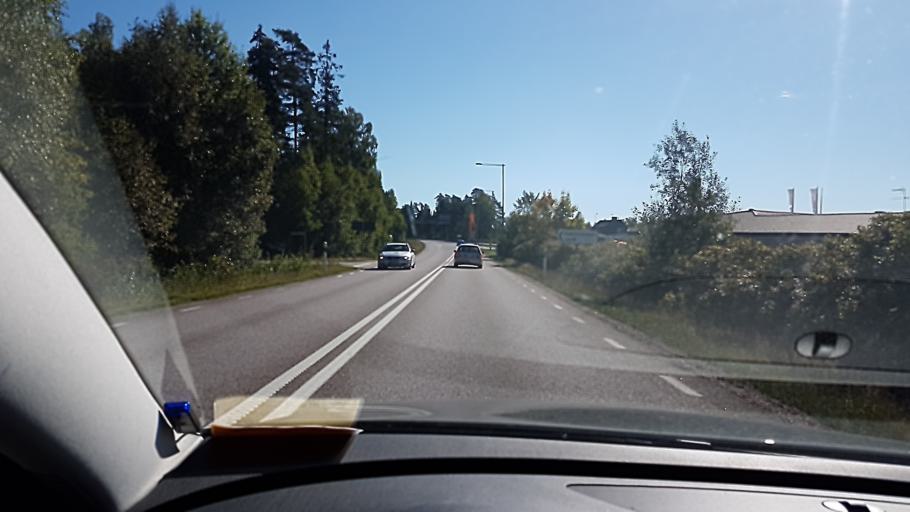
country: SE
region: Kronoberg
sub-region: Lessebo Kommun
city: Hovmantorp
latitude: 56.7870
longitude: 15.1505
